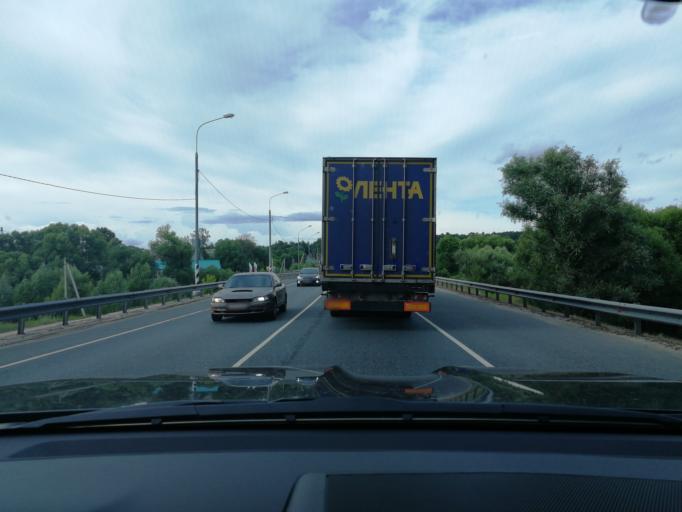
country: RU
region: Moskovskaya
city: Popovo
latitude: 55.0530
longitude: 37.7623
